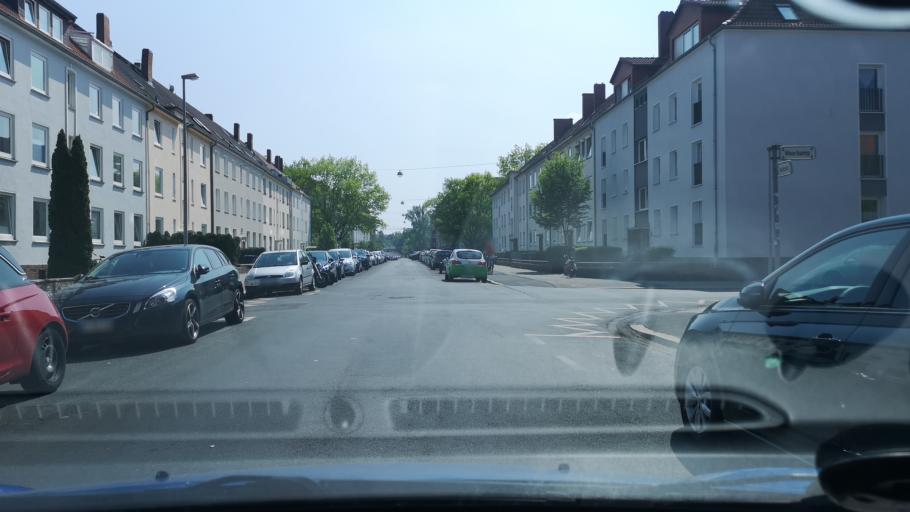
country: DE
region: Lower Saxony
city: Hannover
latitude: 52.3972
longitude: 9.7302
